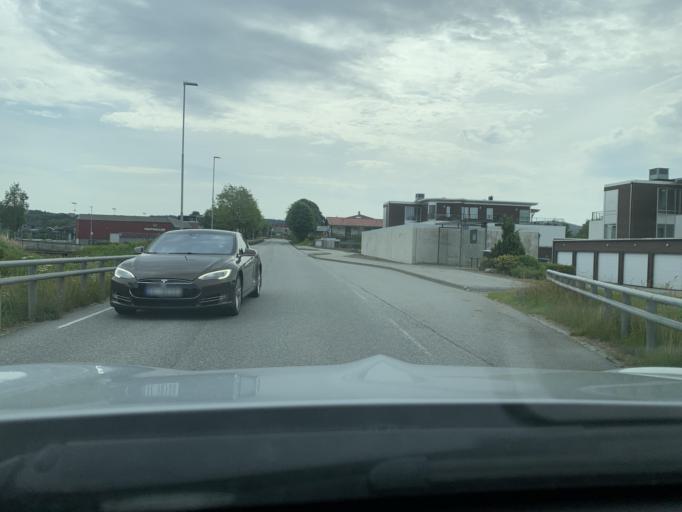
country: NO
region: Rogaland
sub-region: Sandnes
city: Sandnes
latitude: 58.7829
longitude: 5.7155
